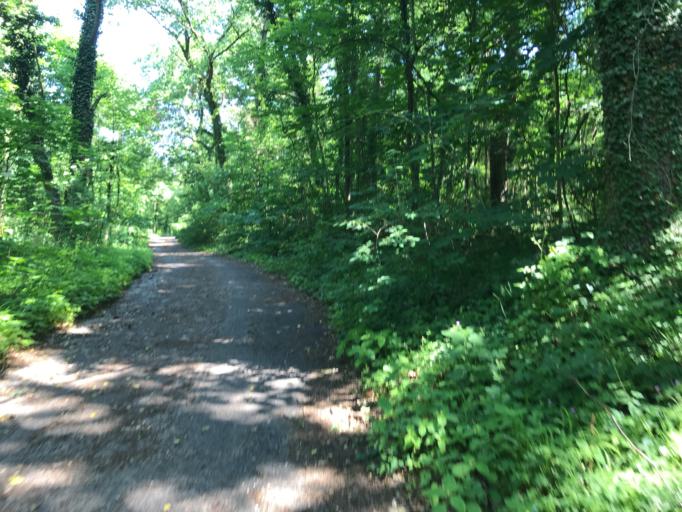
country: DE
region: Rheinland-Pfalz
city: Budenheim
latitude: 50.0017
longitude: 8.1685
